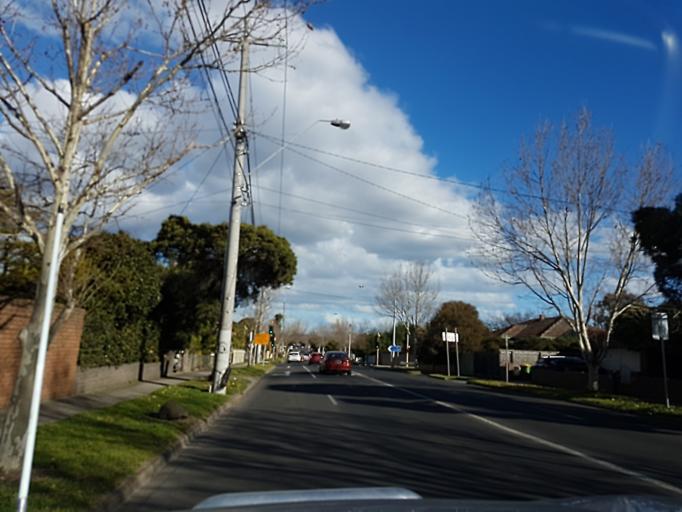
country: AU
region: Victoria
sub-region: Darebin
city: Fairfield
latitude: -37.7718
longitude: 145.0265
